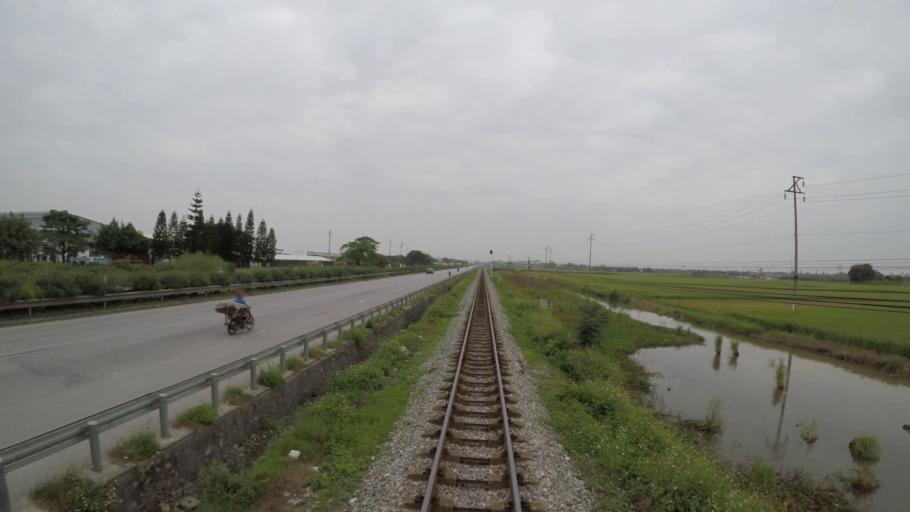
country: VN
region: Hai Duong
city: Phu Thai
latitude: 20.9639
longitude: 106.5166
